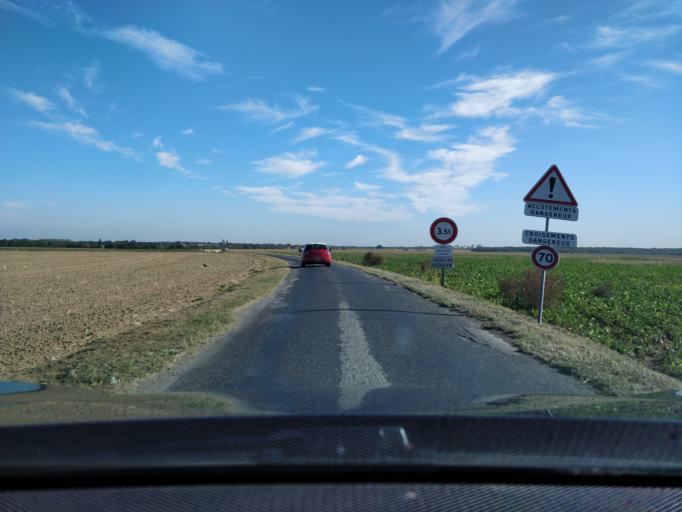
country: FR
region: Ile-de-France
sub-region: Departement de l'Essonne
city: Gometz-la-Ville
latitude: 48.6549
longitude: 2.1121
